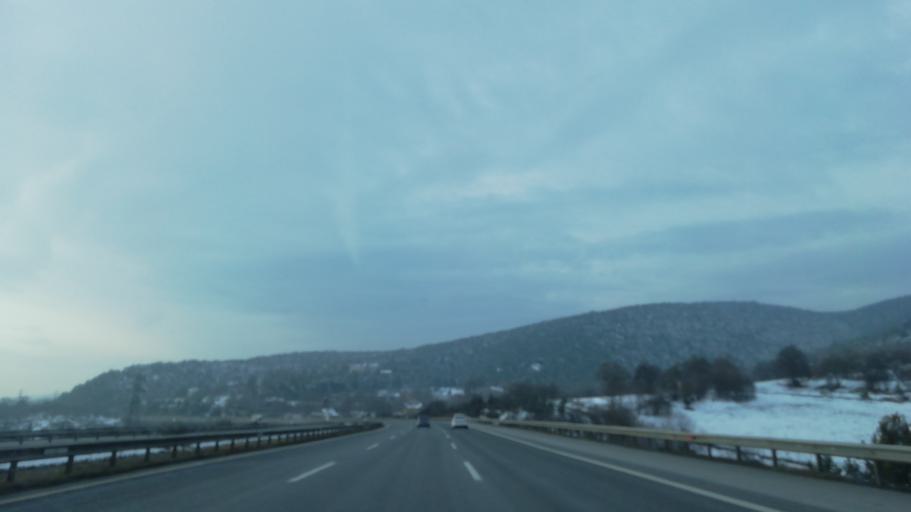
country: TR
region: Bolu
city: Bolu
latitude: 40.7611
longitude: 31.5924
